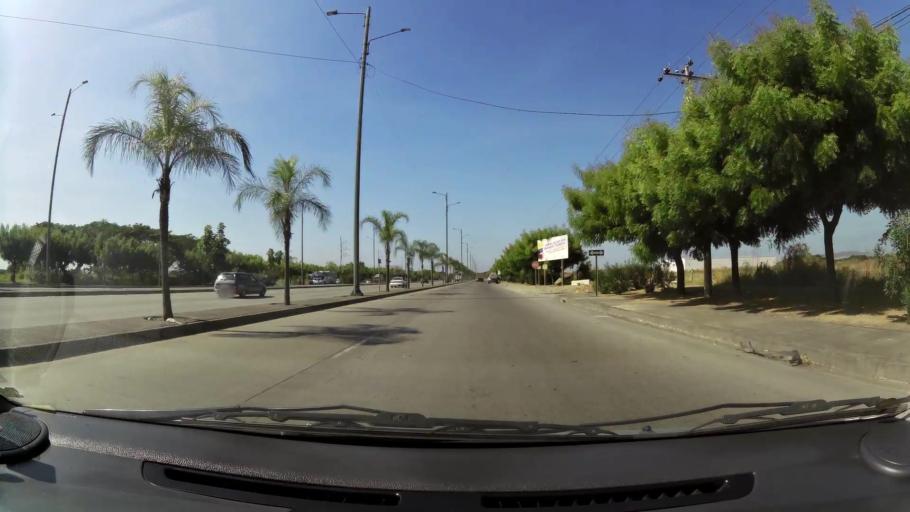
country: EC
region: Guayas
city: Eloy Alfaro
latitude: -2.1013
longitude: -79.8895
